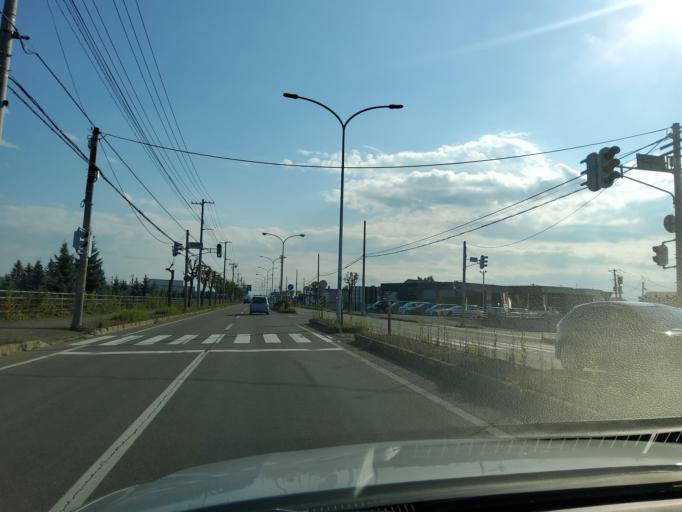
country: JP
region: Hokkaido
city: Obihiro
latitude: 42.8854
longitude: 143.2027
